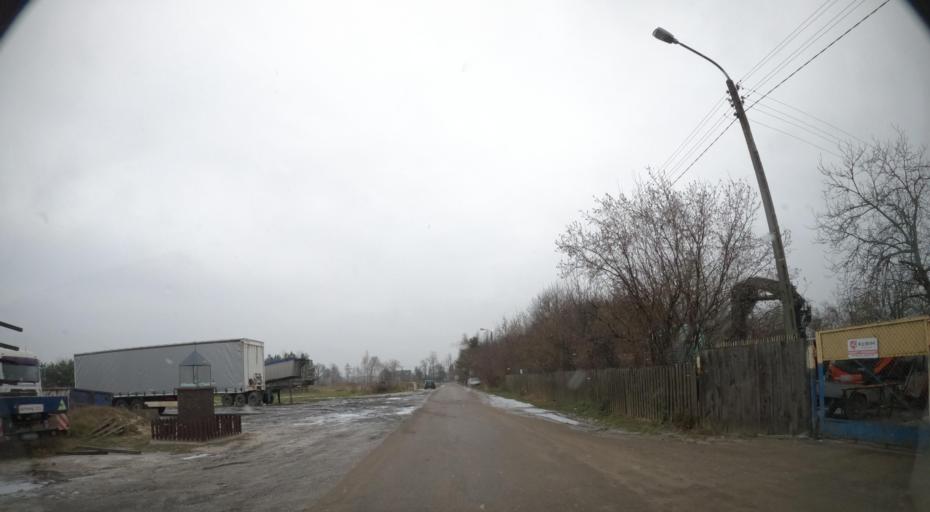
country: PL
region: Masovian Voivodeship
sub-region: Powiat radomski
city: Jedlnia-Letnisko
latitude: 51.3947
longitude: 21.2703
